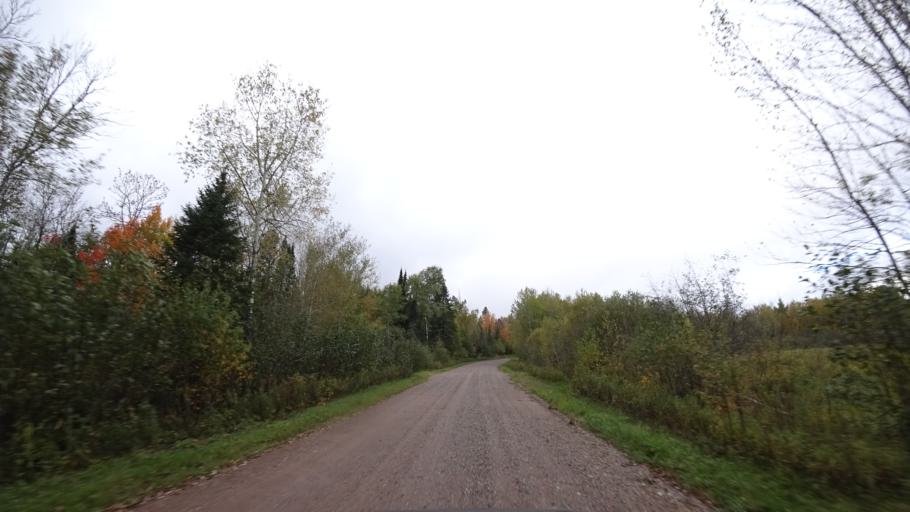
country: US
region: Wisconsin
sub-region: Sawyer County
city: Little Round Lake
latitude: 45.9780
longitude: -90.9943
